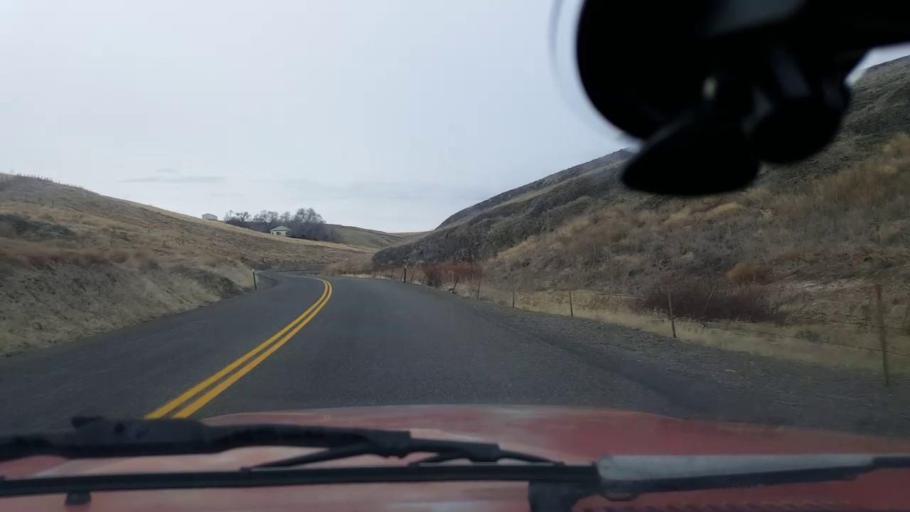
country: US
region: Washington
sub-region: Asotin County
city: Clarkston Heights-Vineland
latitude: 46.3820
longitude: -117.1281
